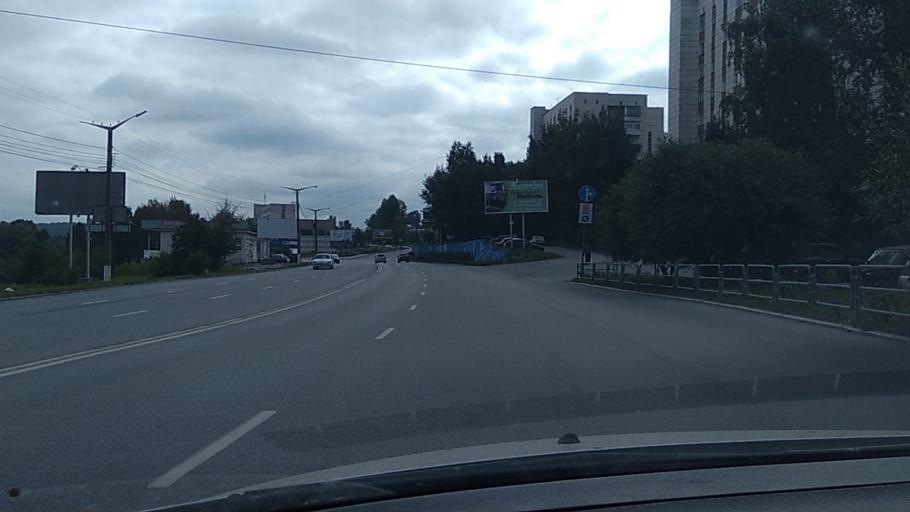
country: RU
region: Chelyabinsk
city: Zlatoust
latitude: 55.1707
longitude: 59.6726
